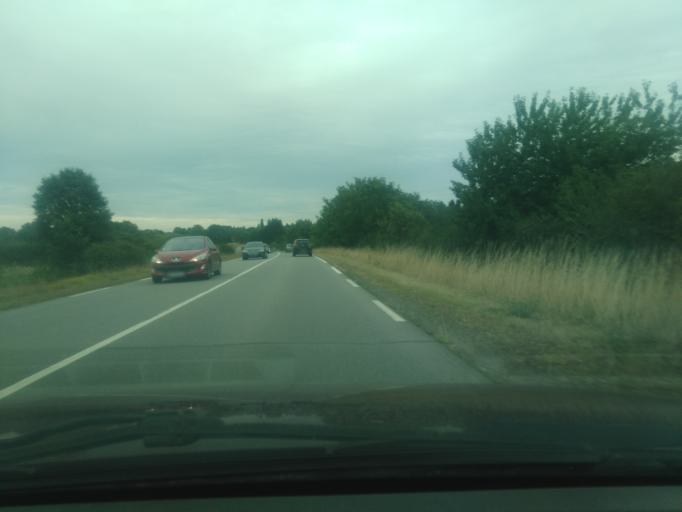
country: FR
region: Centre
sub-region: Departement de l'Indre
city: Saint-Gaultier
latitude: 46.6400
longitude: 1.4051
